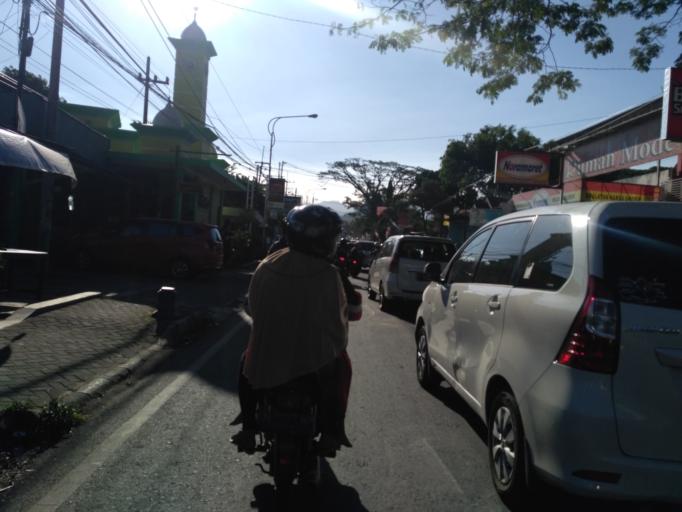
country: ID
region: East Java
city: Batu
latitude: -7.9155
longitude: 112.5868
